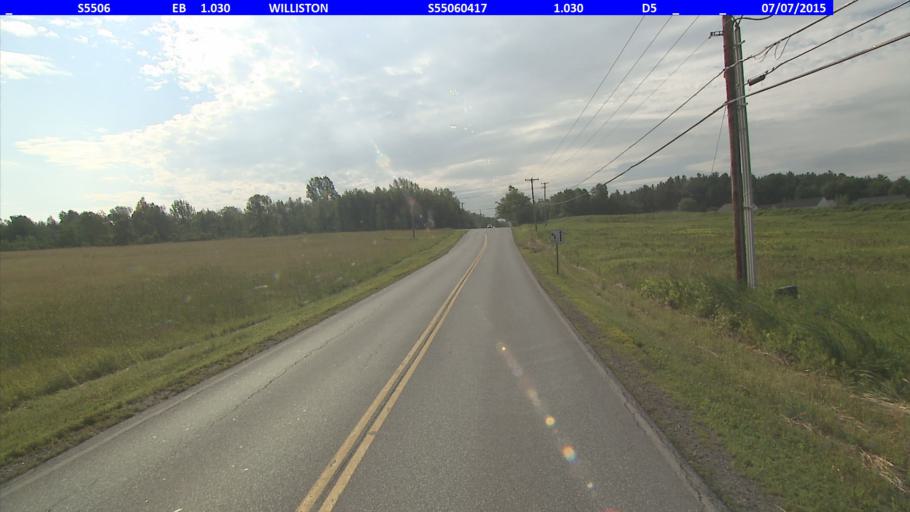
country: US
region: Vermont
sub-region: Chittenden County
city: Essex Junction
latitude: 44.4622
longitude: -73.0937
